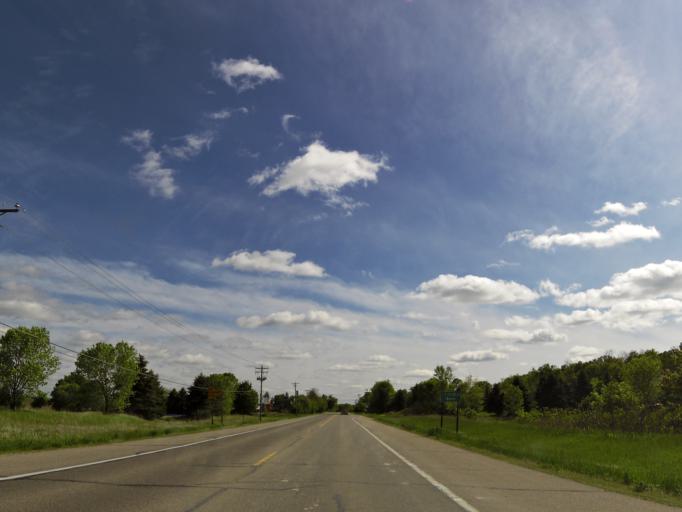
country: US
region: Wisconsin
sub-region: Saint Croix County
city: Hudson
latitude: 44.9821
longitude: -92.7909
